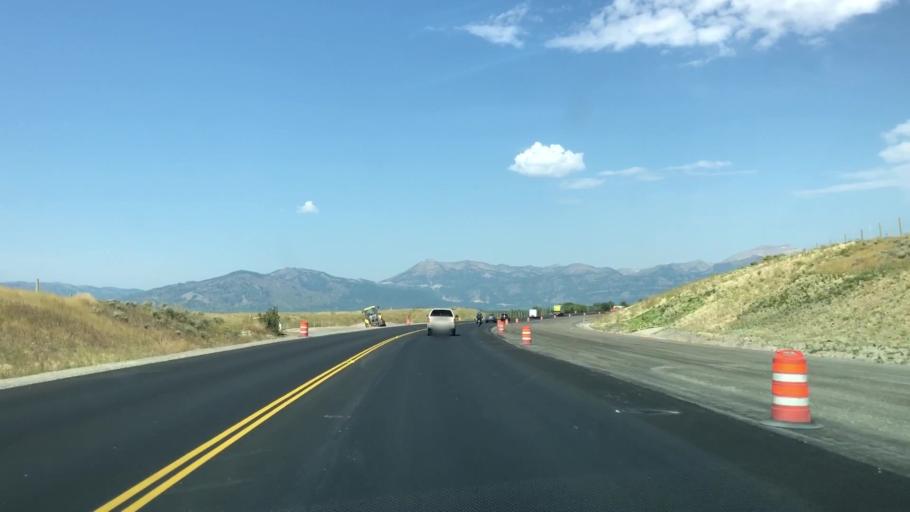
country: US
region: Wyoming
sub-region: Teton County
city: South Park
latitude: 43.4097
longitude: -110.7685
